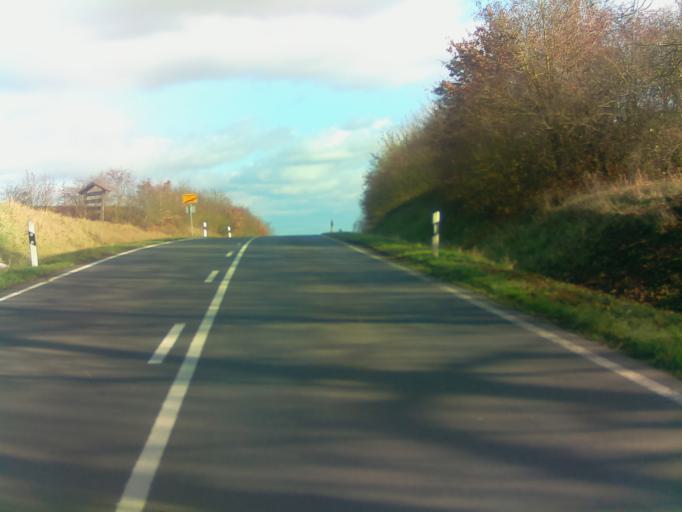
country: DE
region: Thuringia
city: Gleichamberg
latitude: 50.3470
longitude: 10.6075
